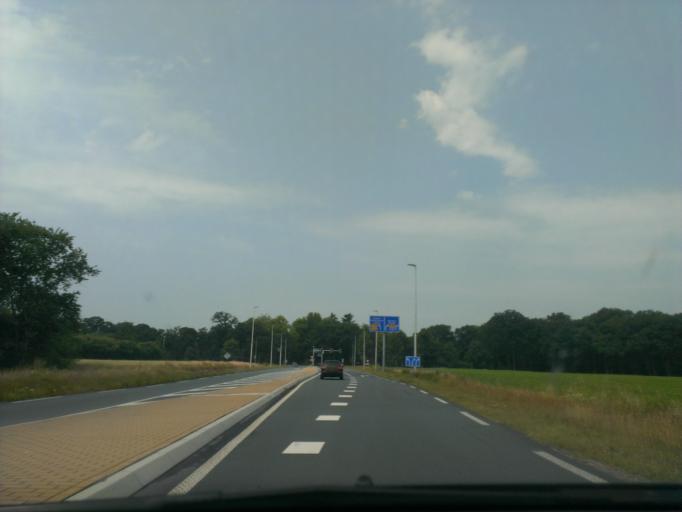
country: NL
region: Overijssel
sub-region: Gemeente Wierden
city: Wierden
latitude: 52.3210
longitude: 6.5431
